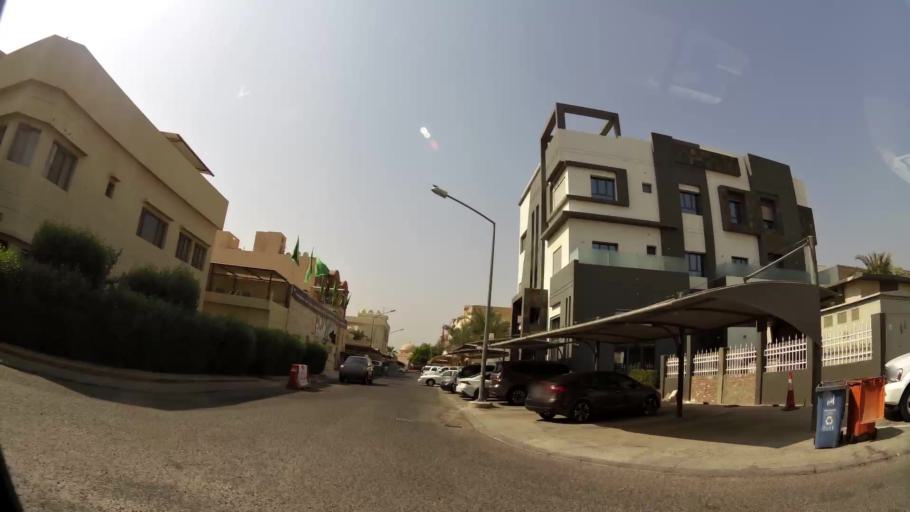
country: KW
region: Al Asimah
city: Ad Dasmah
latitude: 29.3535
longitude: 48.0132
